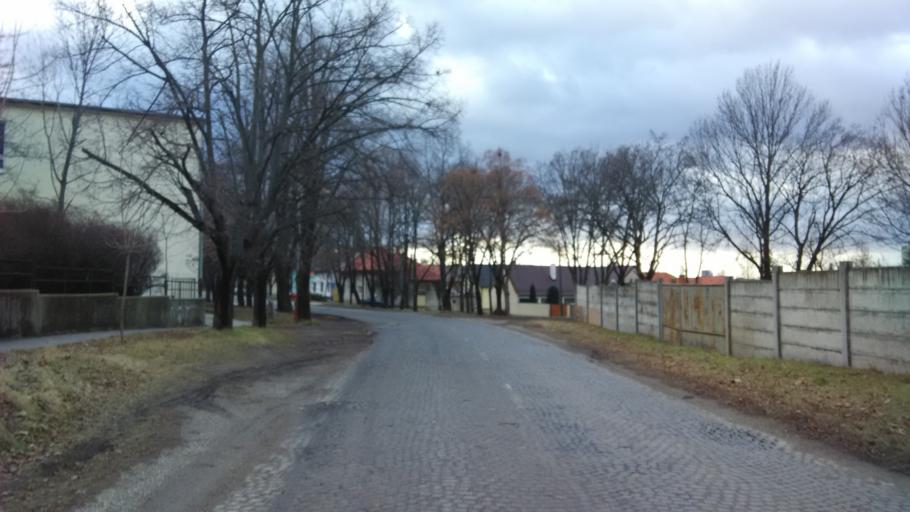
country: SK
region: Nitriansky
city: Zlate Moravce
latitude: 48.3861
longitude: 18.4002
